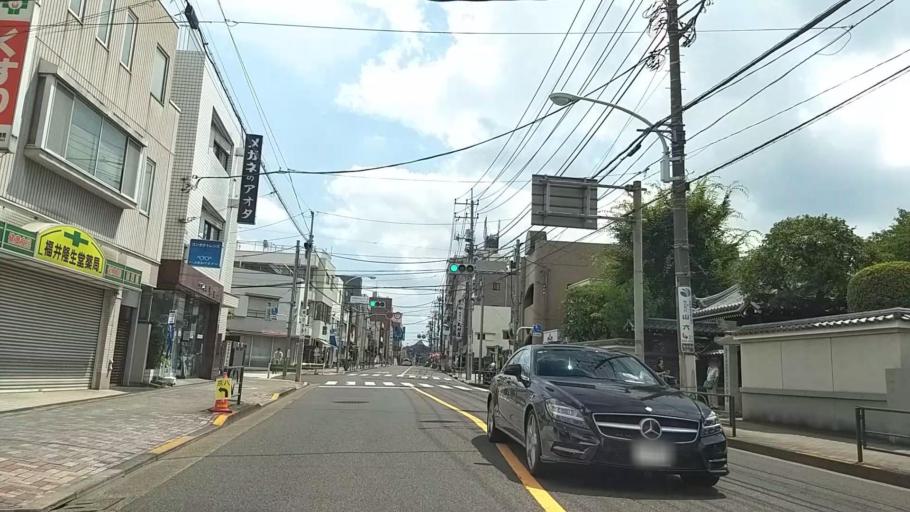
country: JP
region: Tokyo
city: Hachioji
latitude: 35.6629
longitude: 139.3234
